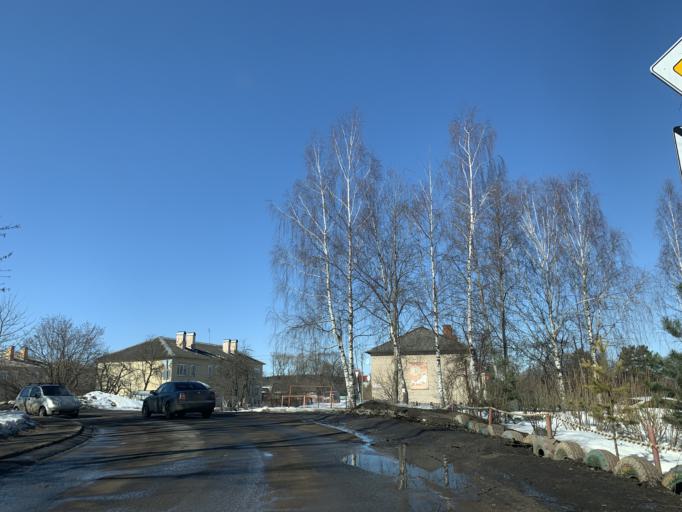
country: RU
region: Jaroslavl
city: Konstantinovskiy
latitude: 57.8421
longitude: 39.5775
